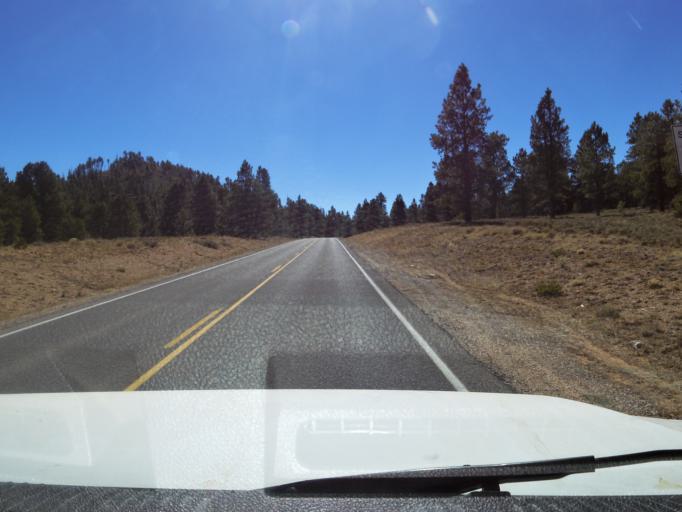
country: US
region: Utah
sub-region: Garfield County
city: Panguitch
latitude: 37.5979
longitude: -112.2084
